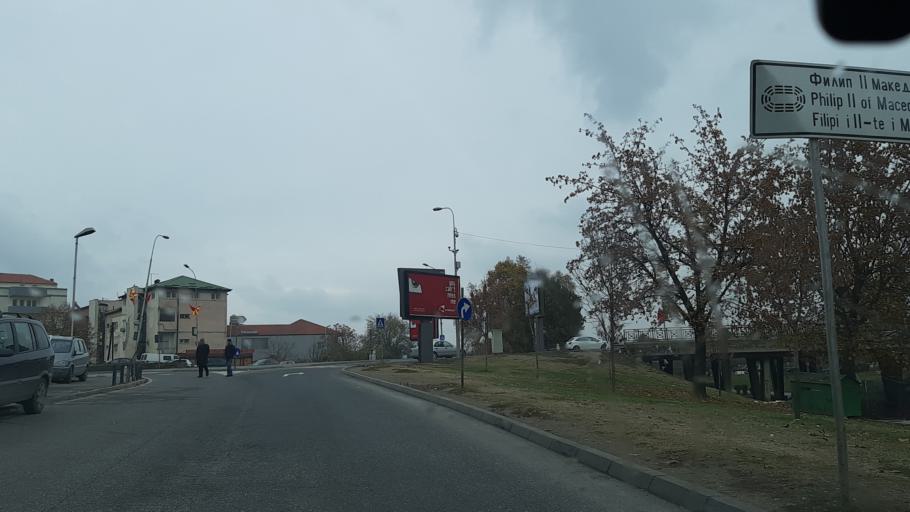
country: MK
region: Cair
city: Cair
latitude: 42.0057
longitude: 21.4403
